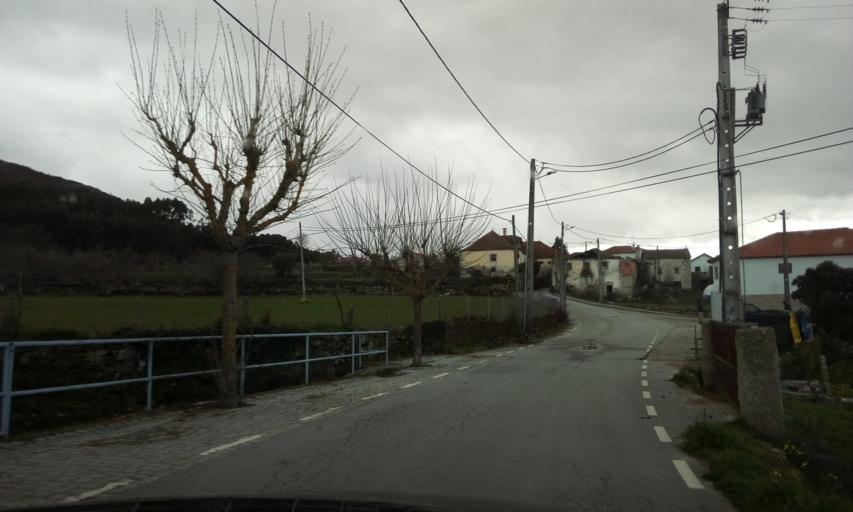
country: PT
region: Guarda
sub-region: Fornos de Algodres
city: Fornos de Algodres
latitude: 40.6391
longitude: -7.5964
